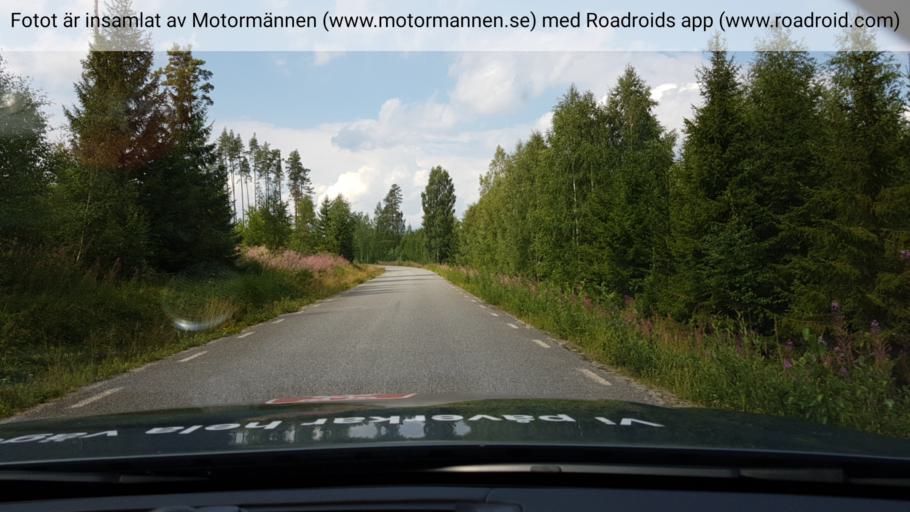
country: SE
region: Jaemtland
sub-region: OEstersunds Kommun
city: Brunflo
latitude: 62.9939
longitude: 15.1133
